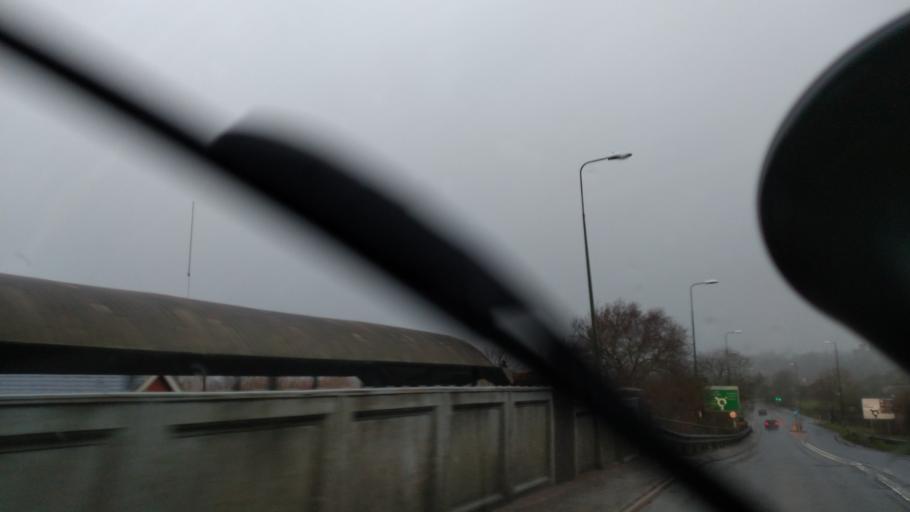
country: GB
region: England
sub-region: West Sussex
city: Arundel
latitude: 50.8483
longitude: -0.5460
